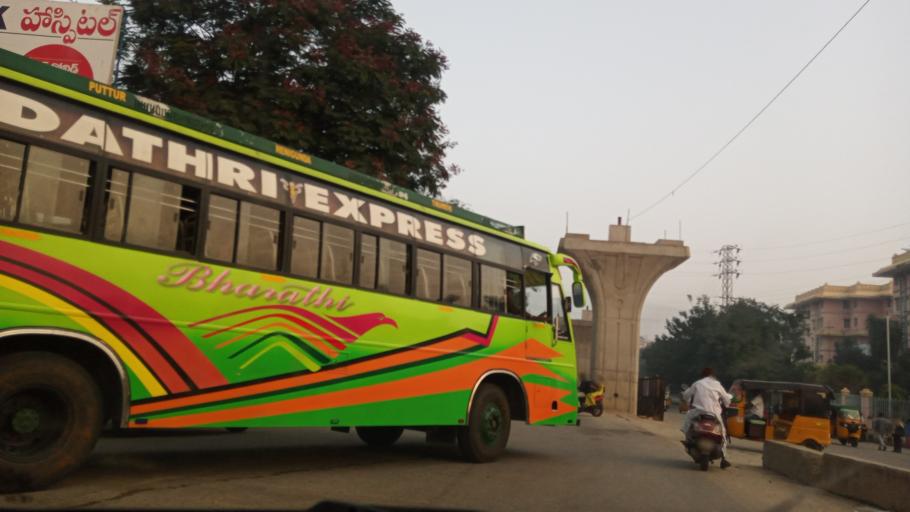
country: IN
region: Andhra Pradesh
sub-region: Chittoor
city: Tirupati
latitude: 13.6306
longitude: 79.4280
